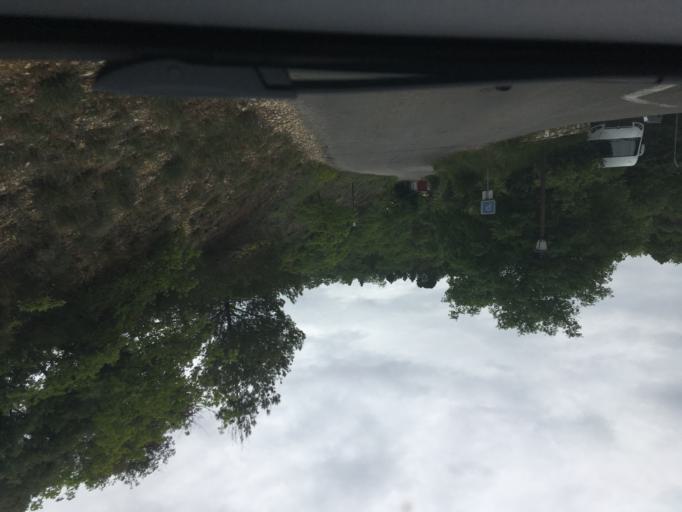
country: FR
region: Provence-Alpes-Cote d'Azur
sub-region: Departement des Alpes-de-Haute-Provence
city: Riez
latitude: 43.7608
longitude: 6.1518
